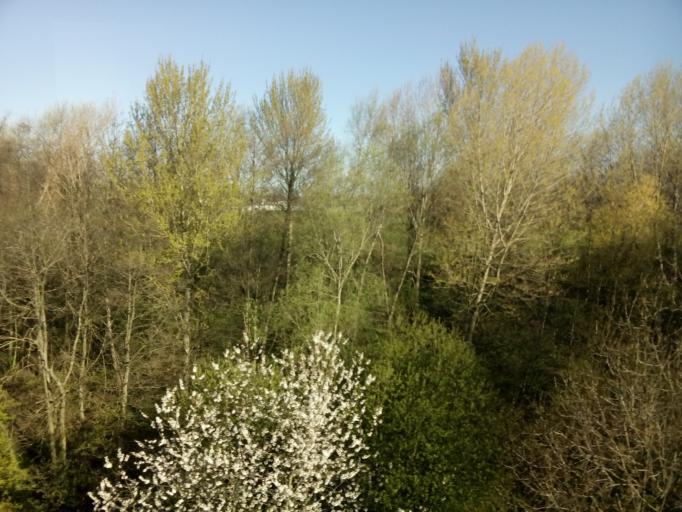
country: GB
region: England
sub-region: Gateshead
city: Gateshead
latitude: 54.9765
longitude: -1.5930
